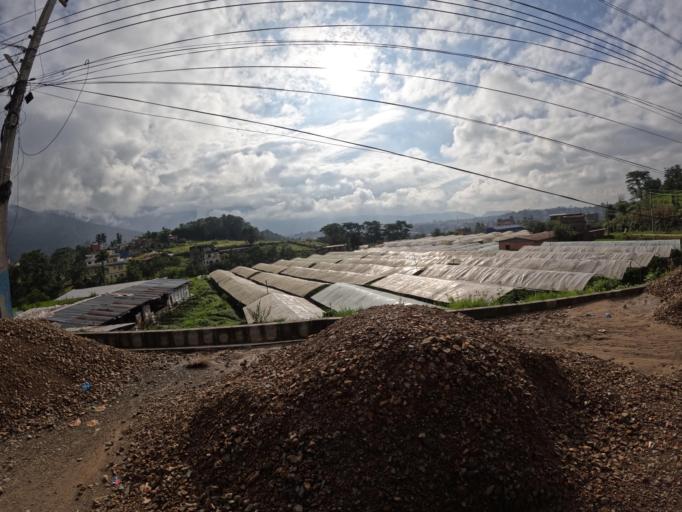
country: NP
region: Central Region
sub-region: Bagmati Zone
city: Kathmandu
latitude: 27.7675
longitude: 85.3315
